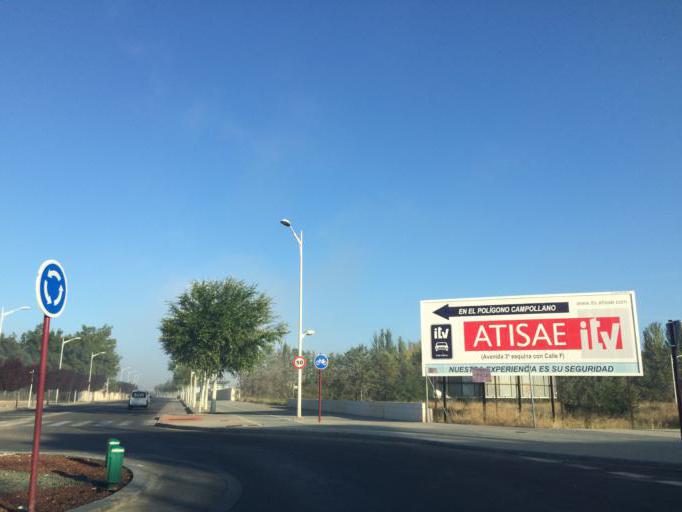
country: ES
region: Castille-La Mancha
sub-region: Provincia de Albacete
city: Albacete
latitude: 39.0039
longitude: -1.8823
